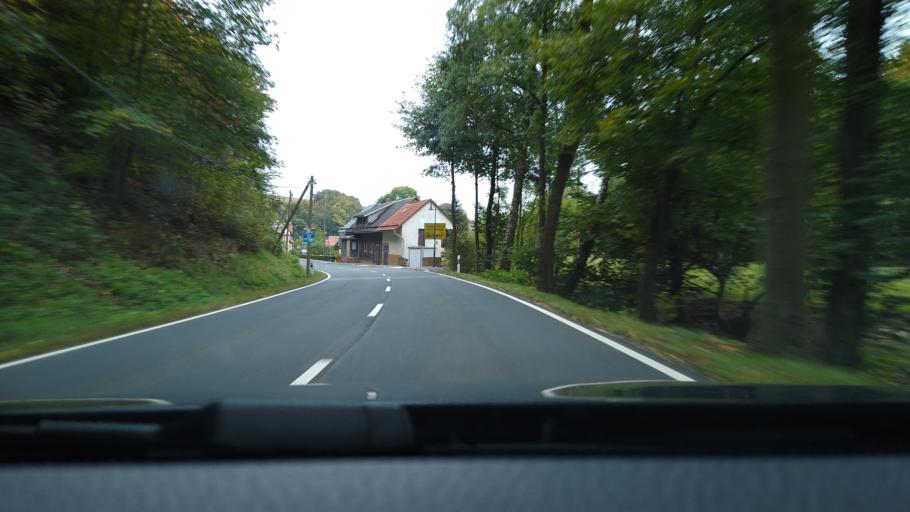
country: DE
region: Thuringia
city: Bachfeld
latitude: 50.4540
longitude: 10.9771
